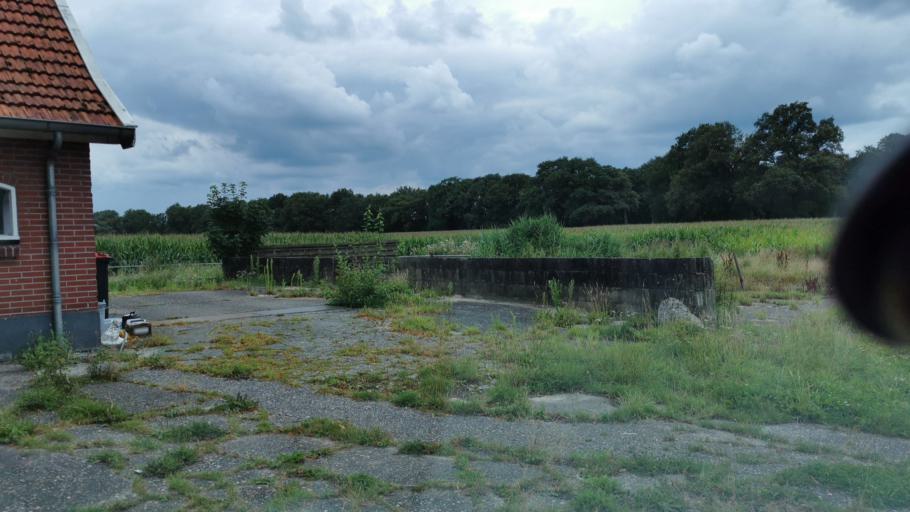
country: NL
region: Overijssel
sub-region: Gemeente Losser
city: Losser
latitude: 52.2367
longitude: 6.9581
